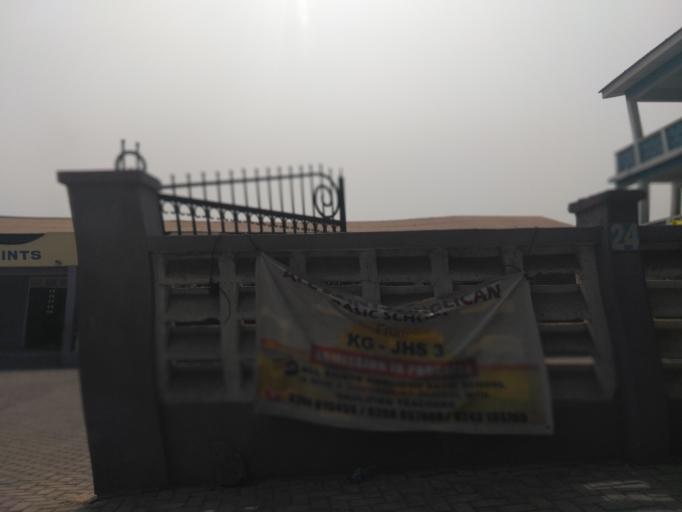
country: GH
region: Ashanti
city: Kumasi
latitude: 6.6762
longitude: -1.6004
